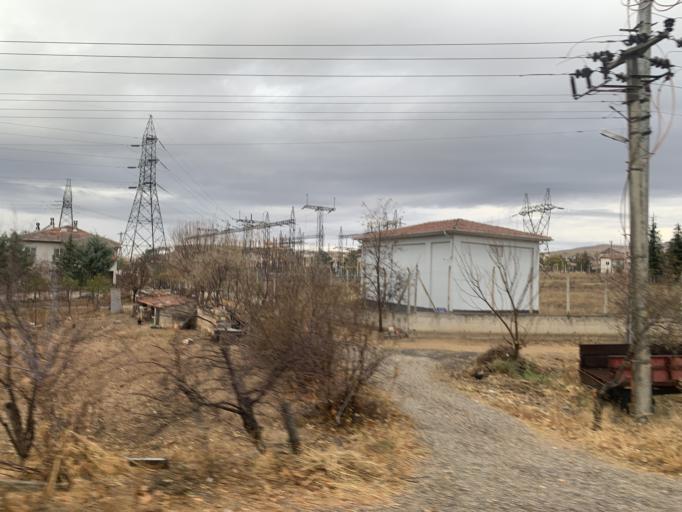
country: TR
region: Nevsehir
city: Avanos
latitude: 38.7201
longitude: 34.8612
